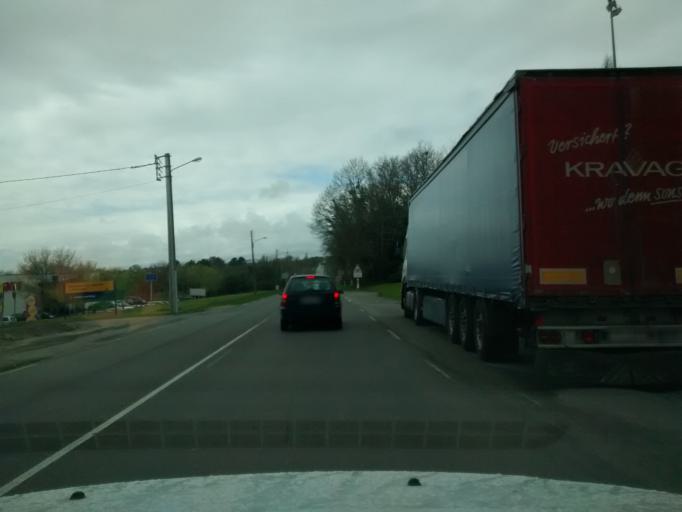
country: FR
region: Brittany
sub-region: Departement du Morbihan
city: Queven
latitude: 47.7680
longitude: -3.4041
